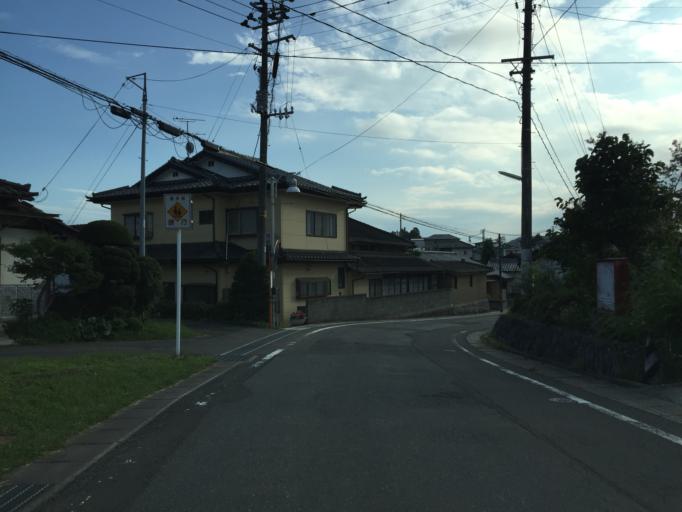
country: JP
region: Fukushima
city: Fukushima-shi
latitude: 37.6578
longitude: 140.5434
